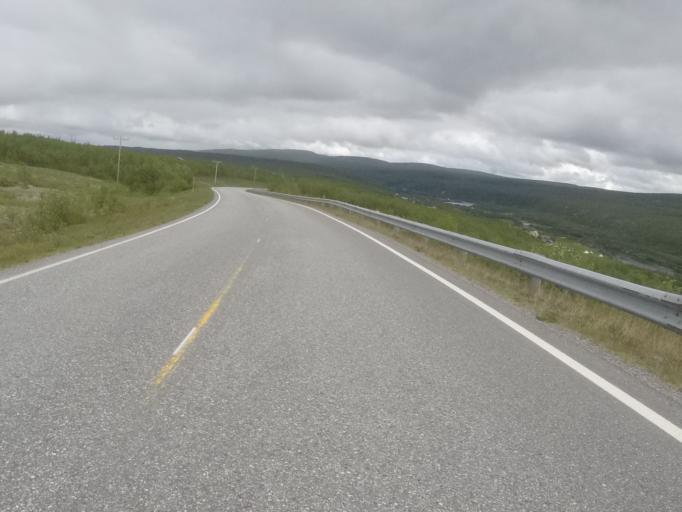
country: NO
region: Finnmark Fylke
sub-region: Alta
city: Alta
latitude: 69.4374
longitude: 23.6450
